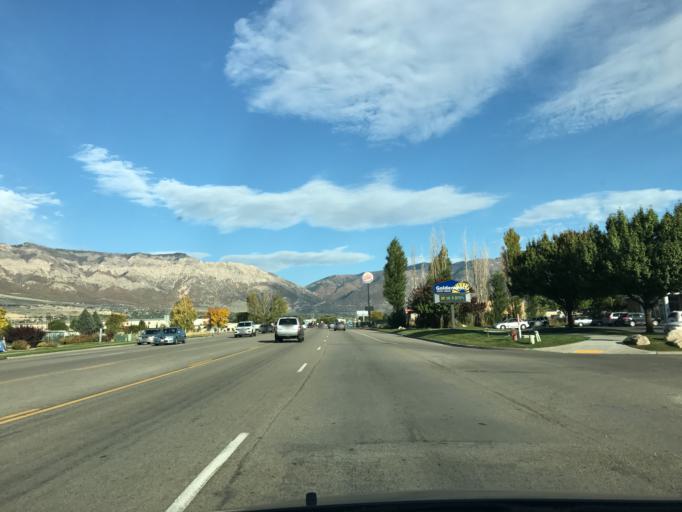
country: US
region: Utah
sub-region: Weber County
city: Farr West
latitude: 41.3065
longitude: -112.0219
